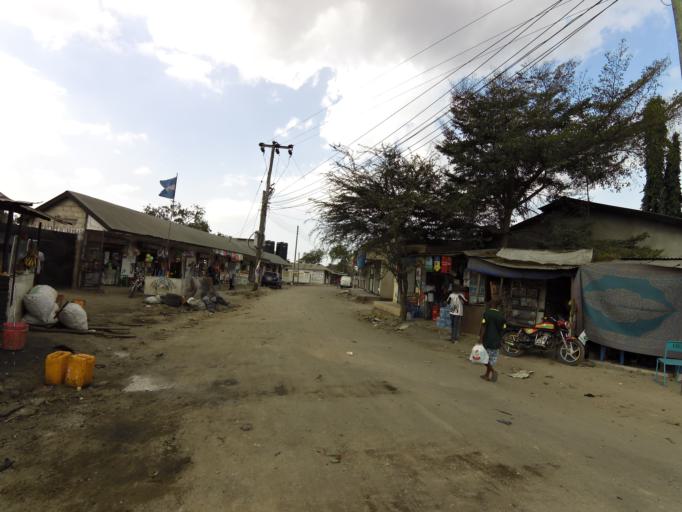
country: TZ
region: Dar es Salaam
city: Magomeni
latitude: -6.8444
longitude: 39.1906
